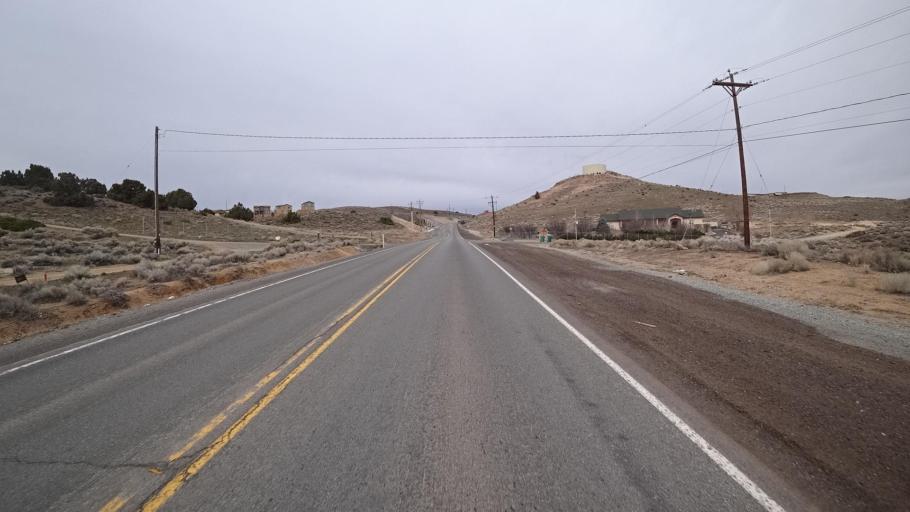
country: US
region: Nevada
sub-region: Washoe County
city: Sun Valley
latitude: 39.6011
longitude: -119.8027
